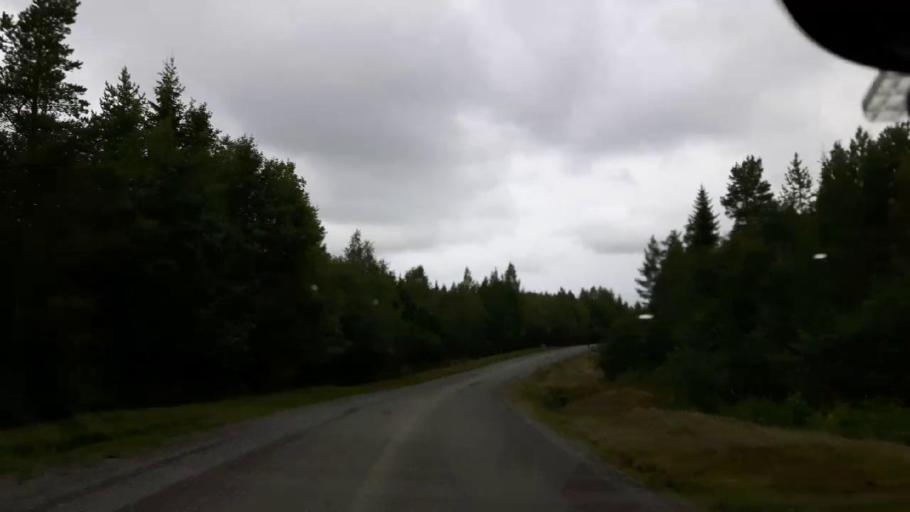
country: SE
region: Jaemtland
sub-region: OEstersunds Kommun
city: Ostersund
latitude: 63.0647
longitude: 14.5520
